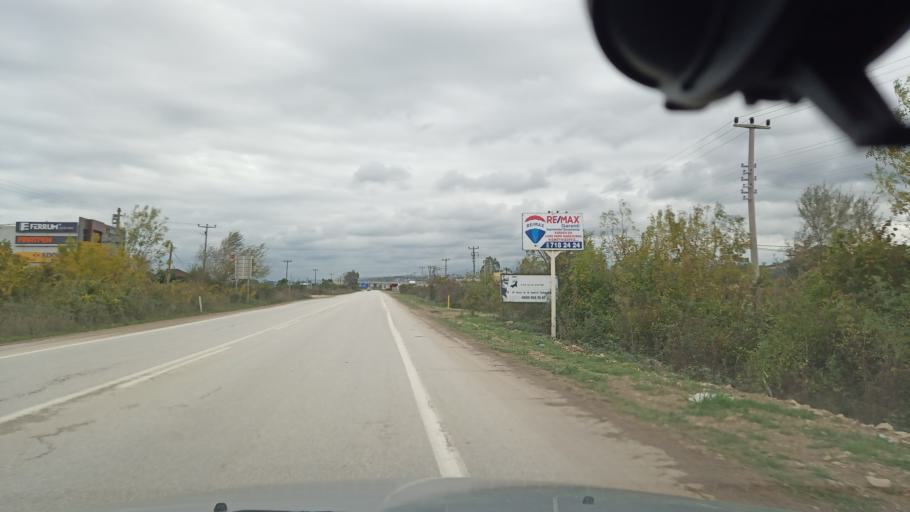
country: TR
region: Sakarya
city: Karasu
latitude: 41.1158
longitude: 30.6533
